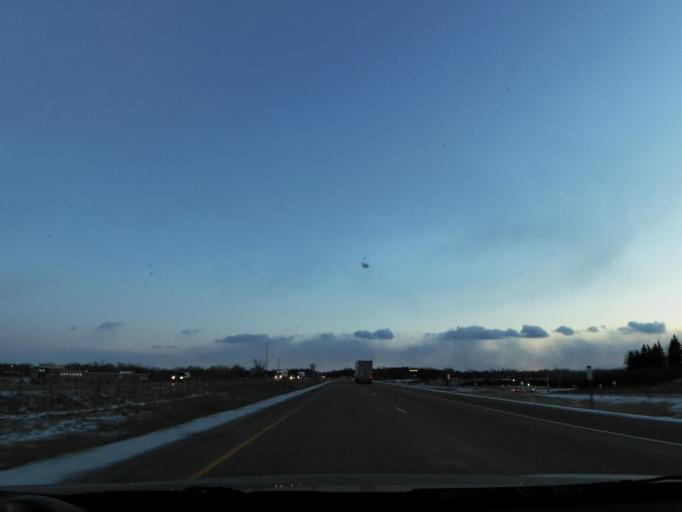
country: US
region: Minnesota
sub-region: Ramsey County
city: North Saint Paul
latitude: 45.0000
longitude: -92.9589
